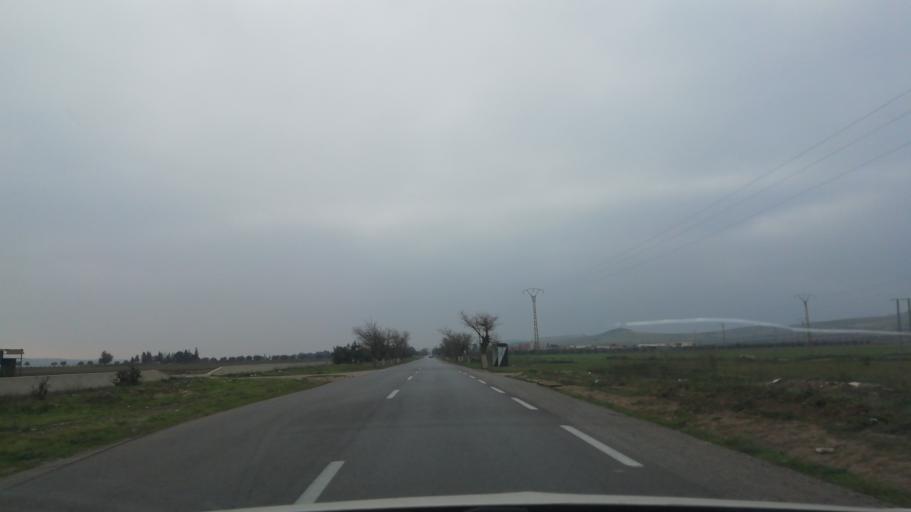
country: DZ
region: Sidi Bel Abbes
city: Sfizef
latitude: 35.2203
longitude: -0.2942
